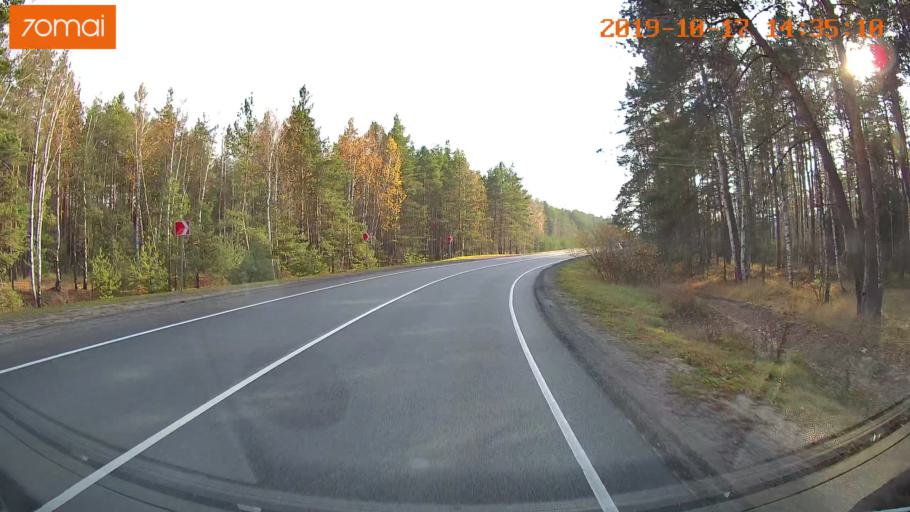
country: RU
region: Rjazan
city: Solotcha
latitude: 54.9033
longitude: 40.0034
